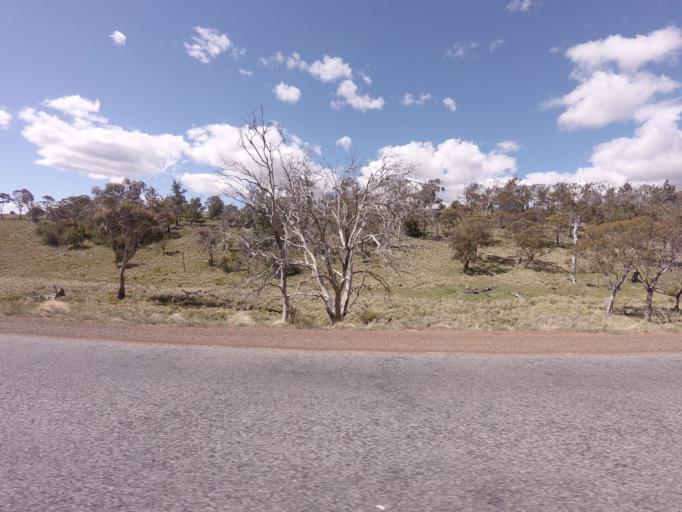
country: AU
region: Tasmania
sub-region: Northern Midlands
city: Evandale
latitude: -41.9363
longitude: 147.5763
